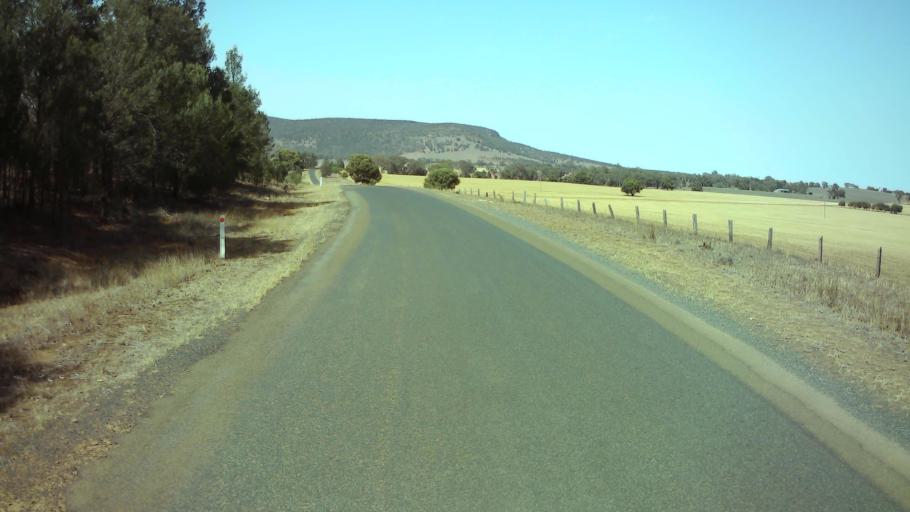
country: AU
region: New South Wales
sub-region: Weddin
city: Grenfell
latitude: -33.8618
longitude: 148.0140
